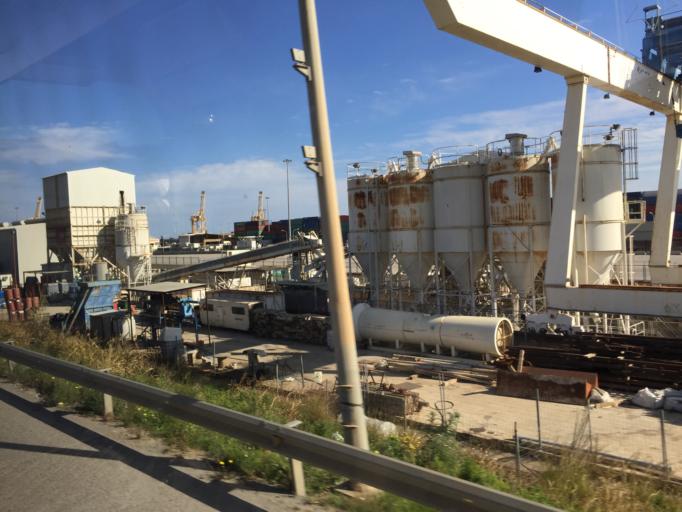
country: ES
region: Catalonia
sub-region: Provincia de Barcelona
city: Sants-Montjuic
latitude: 41.3506
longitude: 2.1508
